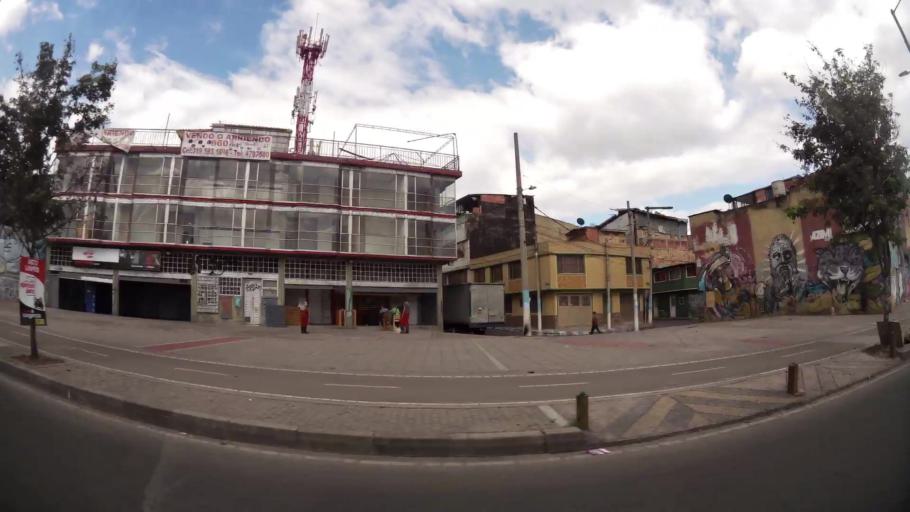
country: CO
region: Cundinamarca
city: Cota
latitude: 4.7240
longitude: -74.0985
